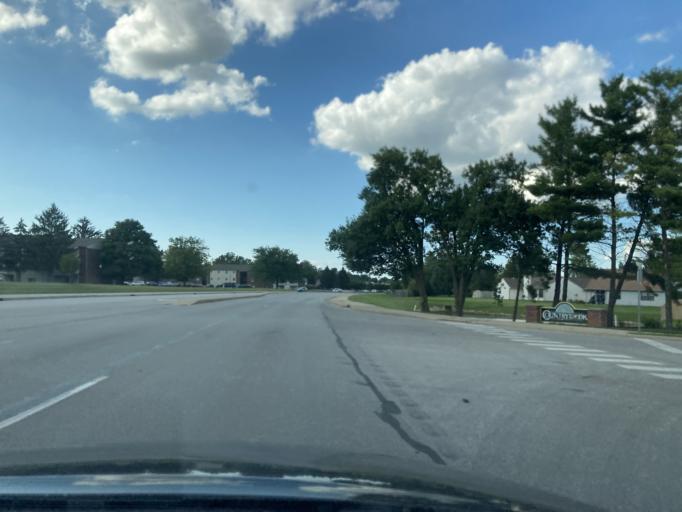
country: US
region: Indiana
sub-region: Marion County
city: Speedway
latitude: 39.8643
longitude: -86.2435
